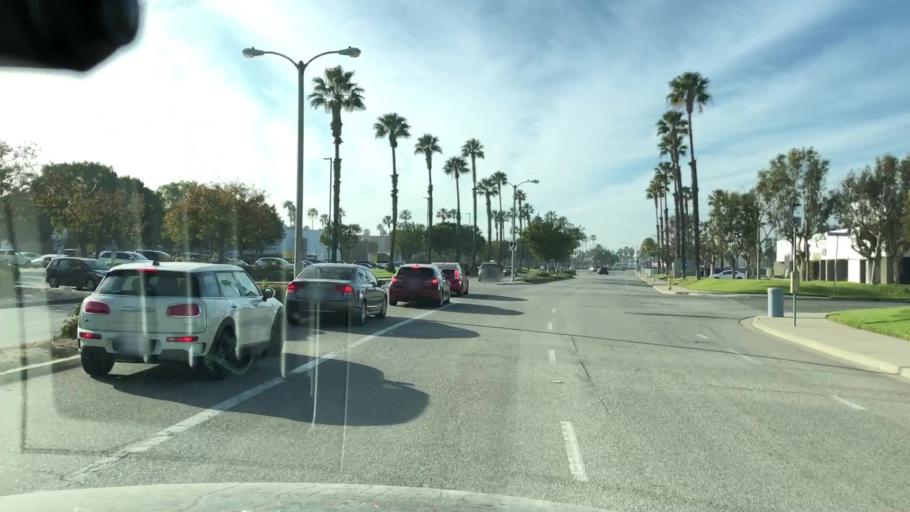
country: US
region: California
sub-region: Ventura County
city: El Rio
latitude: 34.2263
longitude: -119.1460
